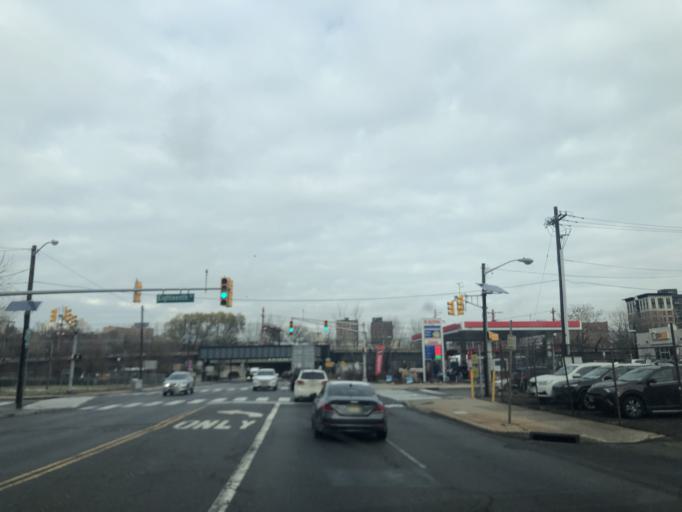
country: US
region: New Jersey
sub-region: Hudson County
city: Hoboken
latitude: 40.7346
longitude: -74.0440
